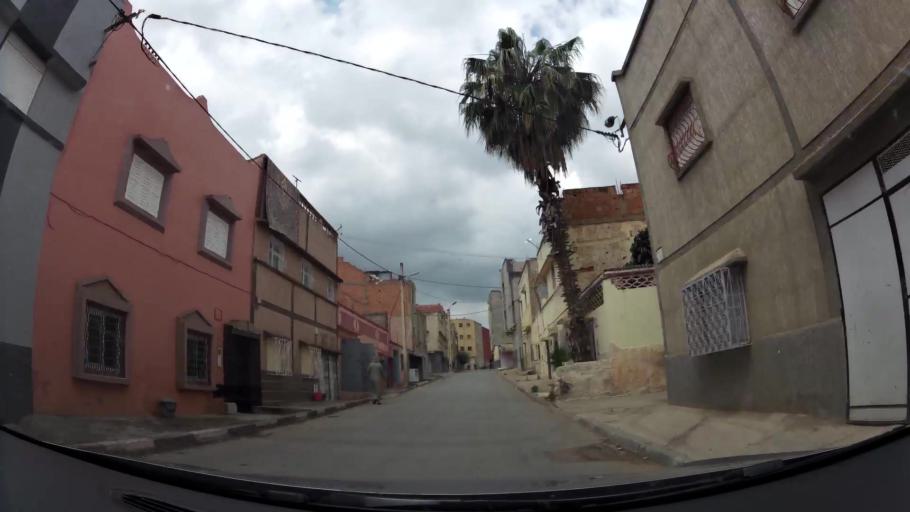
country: MA
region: Rabat-Sale-Zemmour-Zaer
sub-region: Khemisset
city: Tiflet
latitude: 33.8924
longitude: -6.3196
